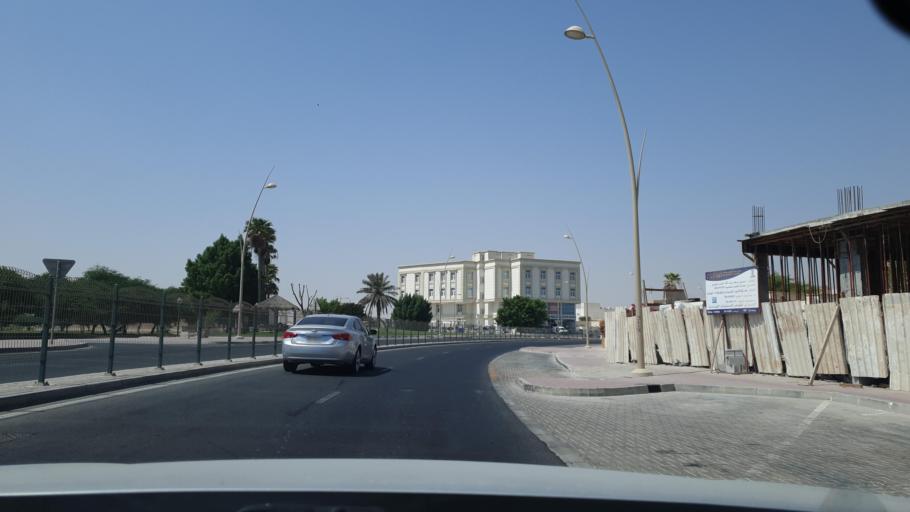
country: QA
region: Al Khawr
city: Al Khawr
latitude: 25.6827
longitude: 51.5135
